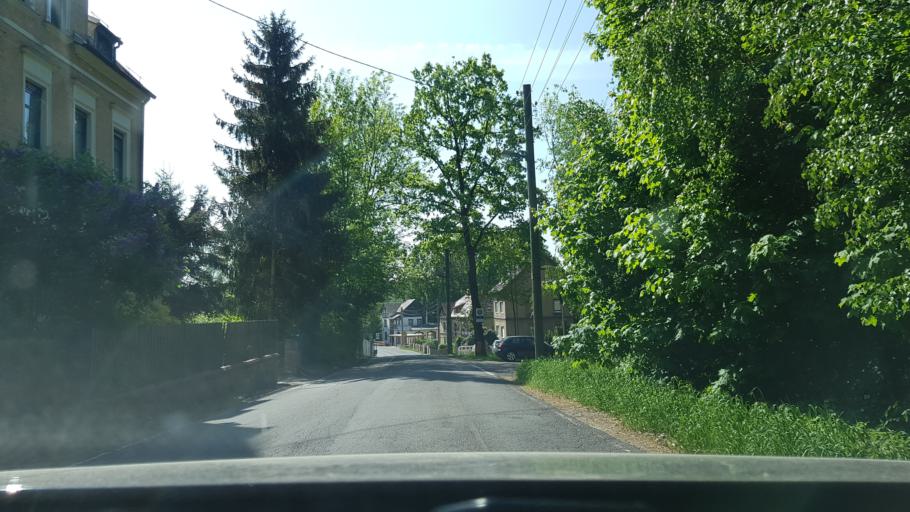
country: DE
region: Saxony
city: Wittgensdorf
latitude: 50.8717
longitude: 12.8746
